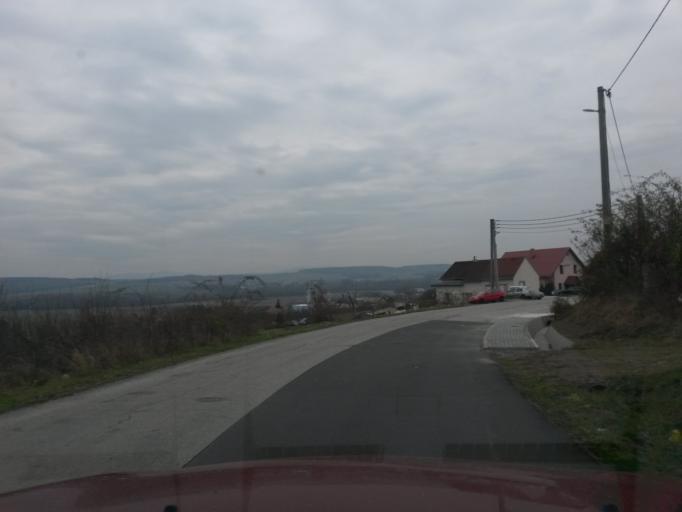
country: SK
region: Kosicky
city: Kosice
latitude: 48.7301
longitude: 21.4444
